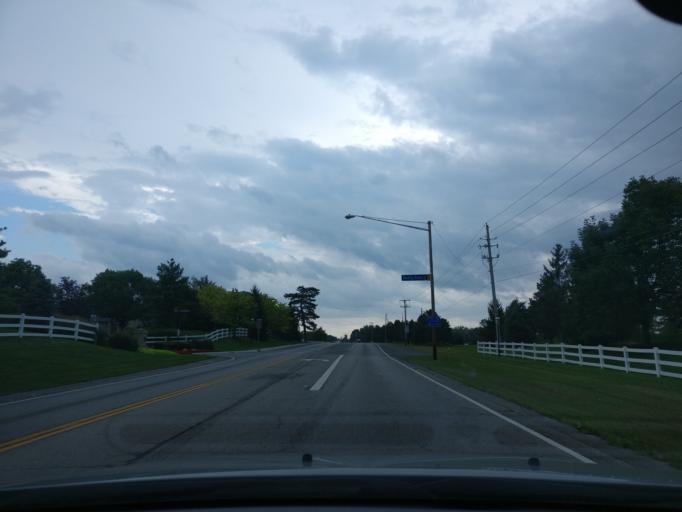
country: US
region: Ohio
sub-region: Warren County
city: Five Points
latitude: 39.6035
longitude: -84.1996
